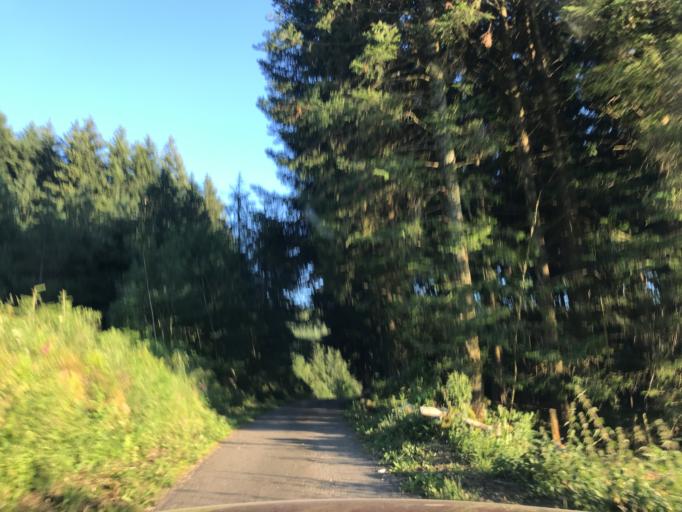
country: FR
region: Rhone-Alpes
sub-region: Departement de la Loire
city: Noiretable
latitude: 45.7819
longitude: 3.6923
